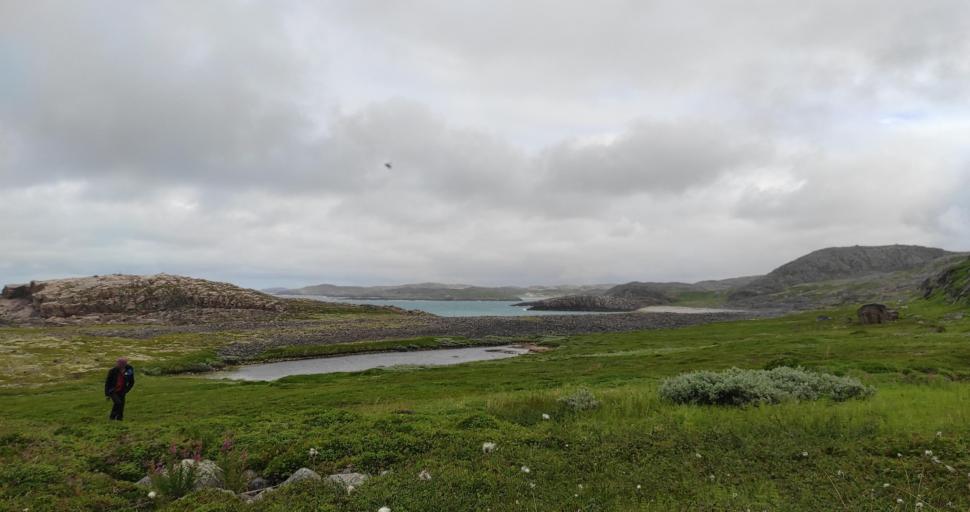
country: RU
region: Murmansk
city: Teriberka
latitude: 69.2188
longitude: 35.5317
